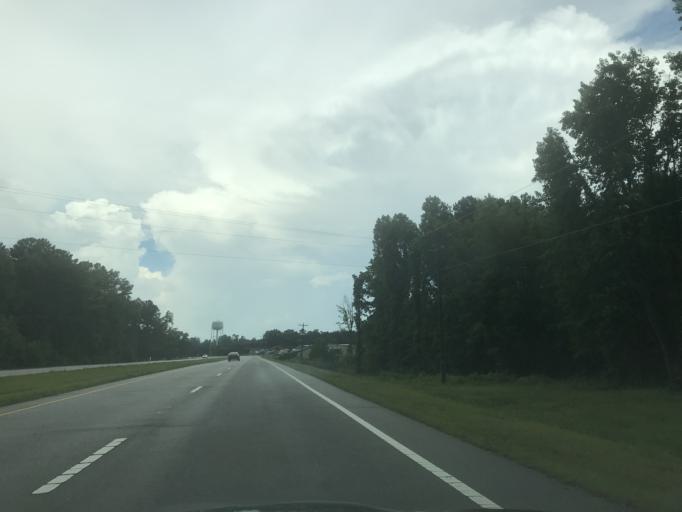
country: US
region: North Carolina
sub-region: Johnston County
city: Wilsons Mills
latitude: 35.5823
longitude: -78.4019
